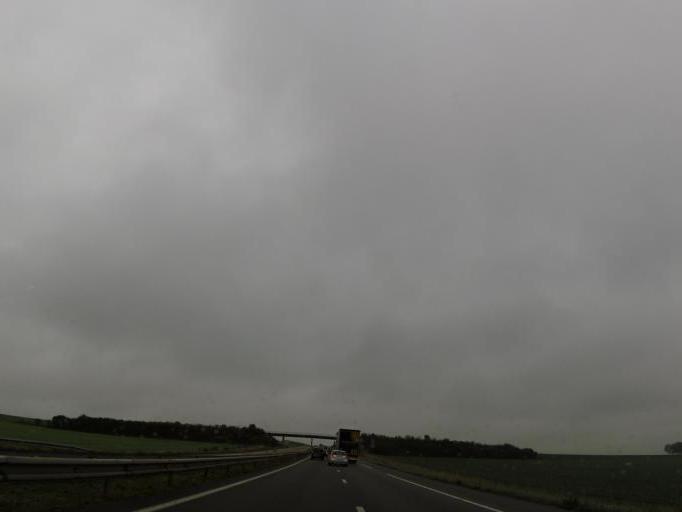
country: FR
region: Champagne-Ardenne
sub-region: Departement de la Marne
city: Verzy
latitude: 49.0865
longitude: 4.2603
